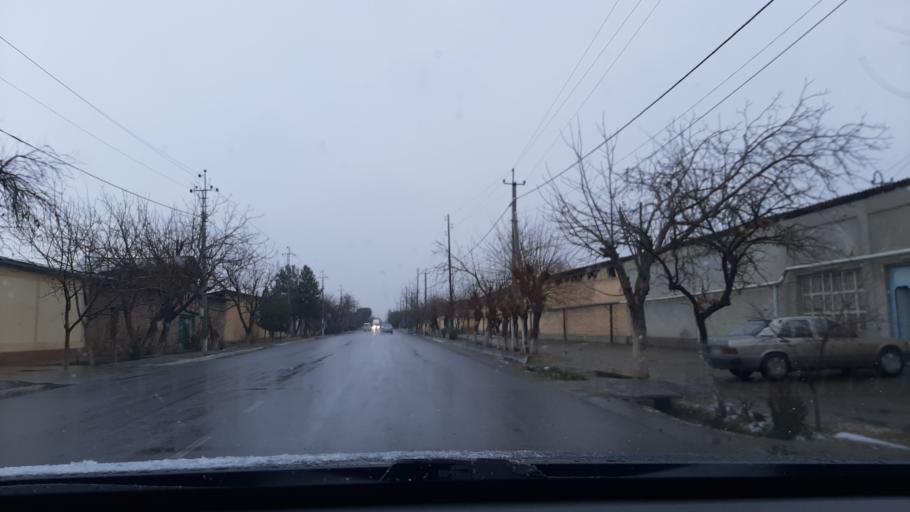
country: TJ
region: Viloyati Sughd
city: Khujand
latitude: 40.2671
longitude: 69.6170
